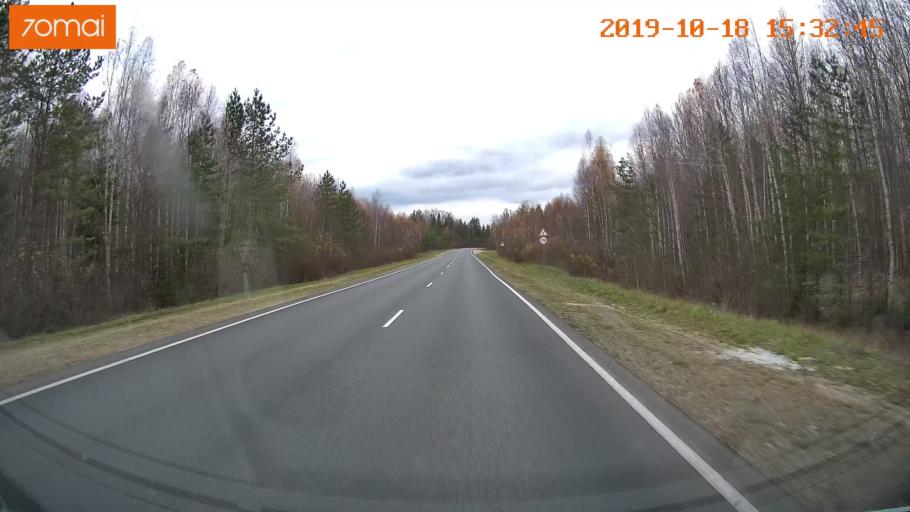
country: RU
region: Vladimir
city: Anopino
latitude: 55.8305
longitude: 40.6479
